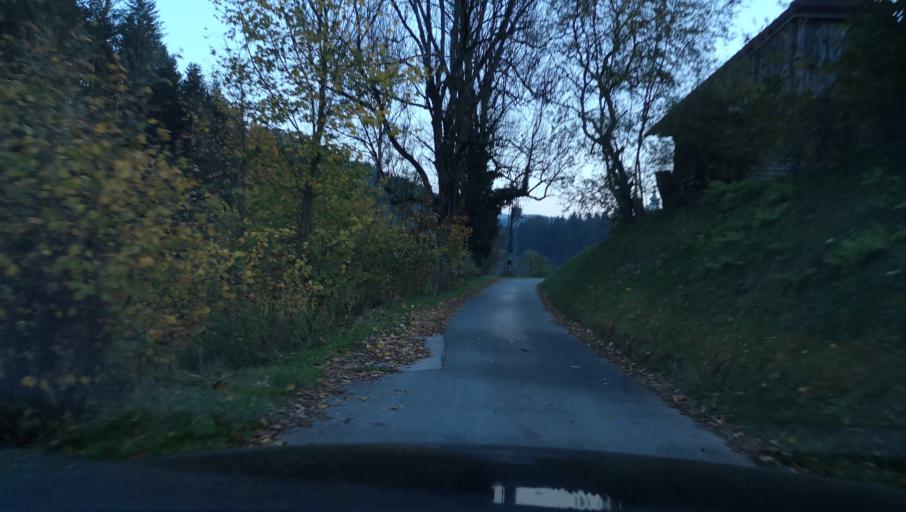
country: AT
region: Styria
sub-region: Politischer Bezirk Weiz
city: Birkfeld
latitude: 47.3445
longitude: 15.6826
